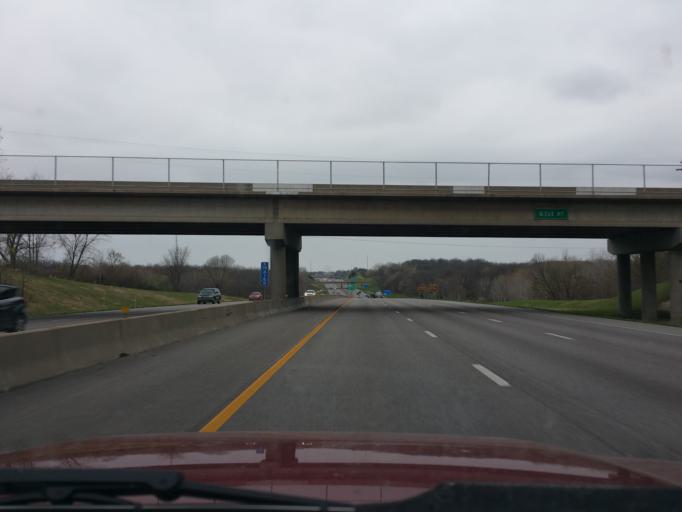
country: US
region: Kansas
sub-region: Johnson County
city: Shawnee
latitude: 39.1055
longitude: -94.7185
